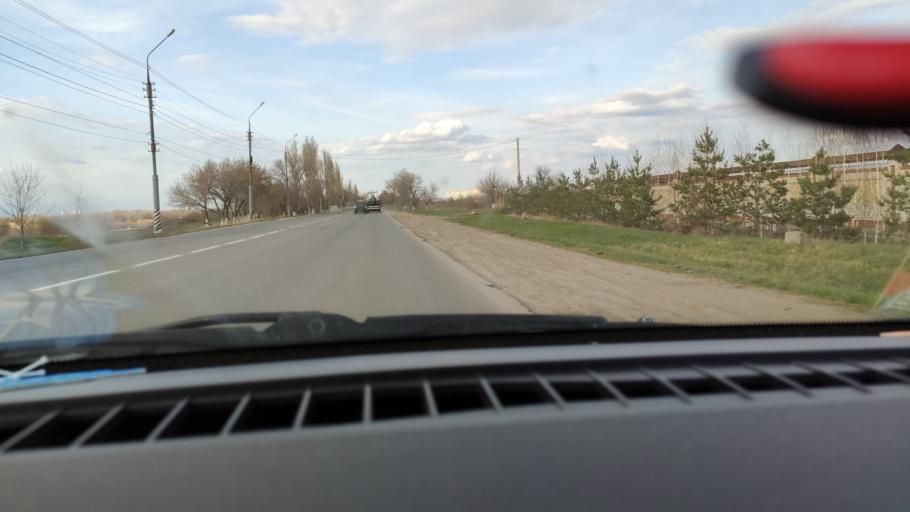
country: RU
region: Saratov
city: Privolzhskiy
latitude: 51.4380
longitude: 46.0640
